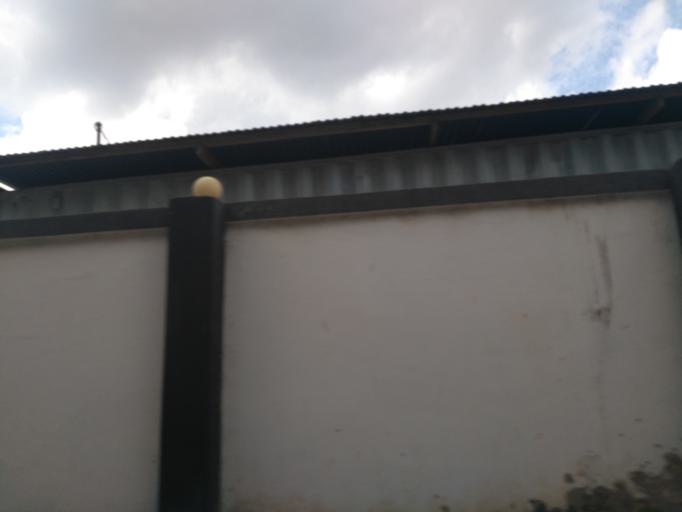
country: TZ
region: Dar es Salaam
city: Magomeni
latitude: -6.7601
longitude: 39.2455
